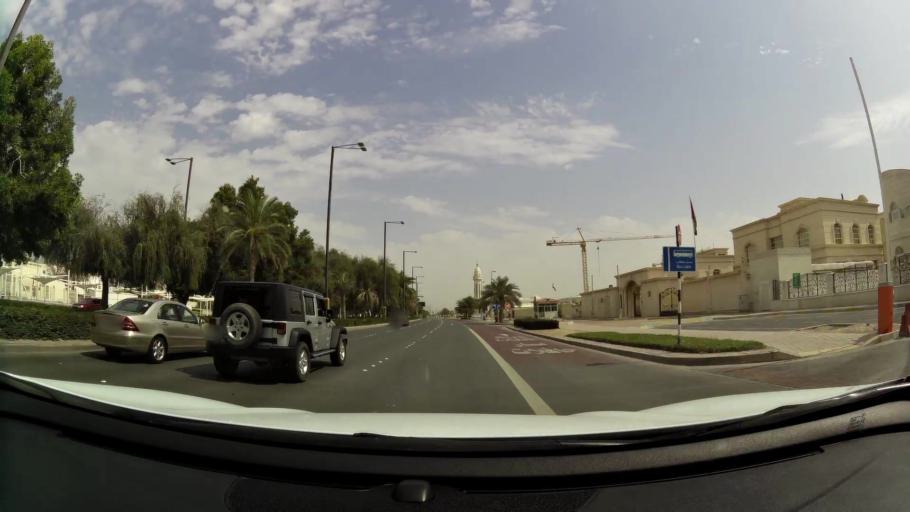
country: AE
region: Abu Dhabi
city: Abu Dhabi
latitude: 24.4564
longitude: 54.3402
